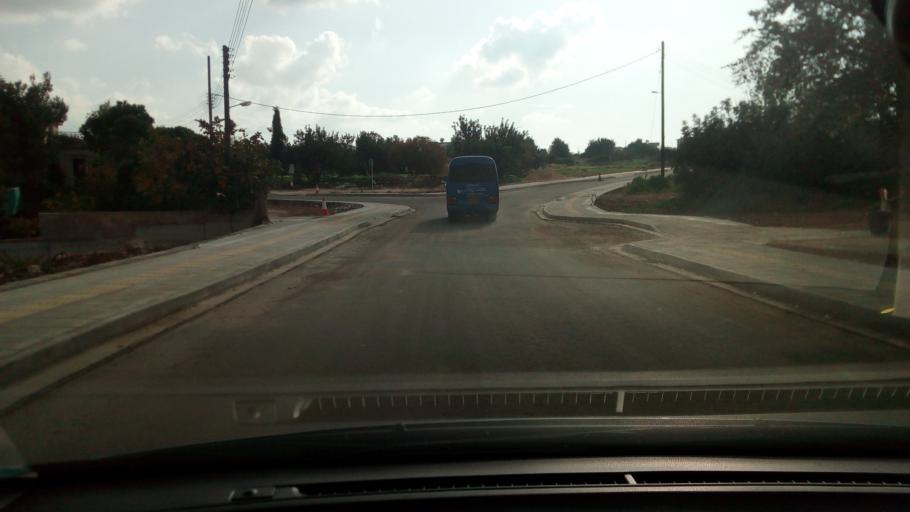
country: CY
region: Pafos
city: Polis
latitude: 35.0304
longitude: 32.3628
